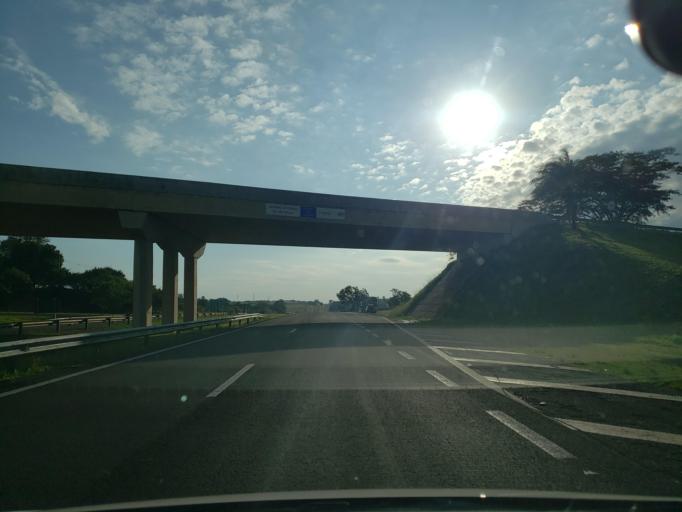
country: BR
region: Sao Paulo
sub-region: Valparaiso
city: Valparaiso
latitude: -21.2122
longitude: -50.8662
